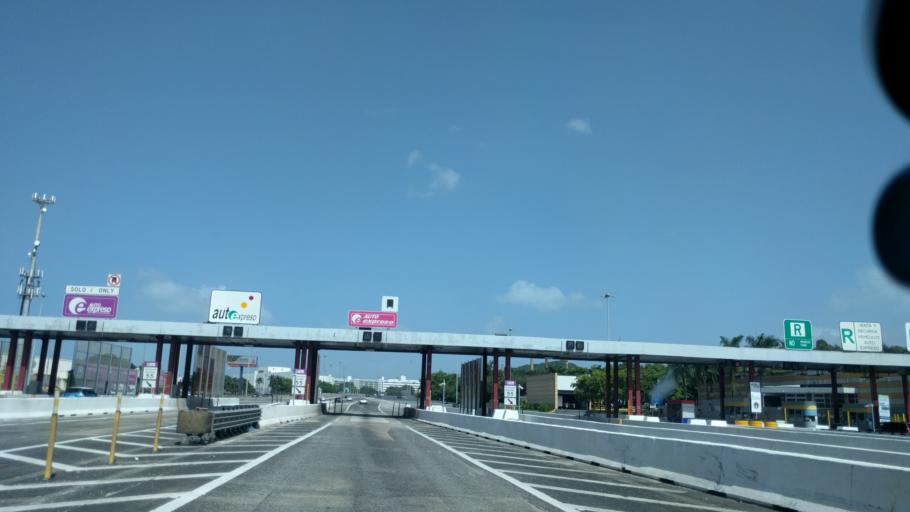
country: PR
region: Catano
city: Catano
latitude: 18.4224
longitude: -66.1200
